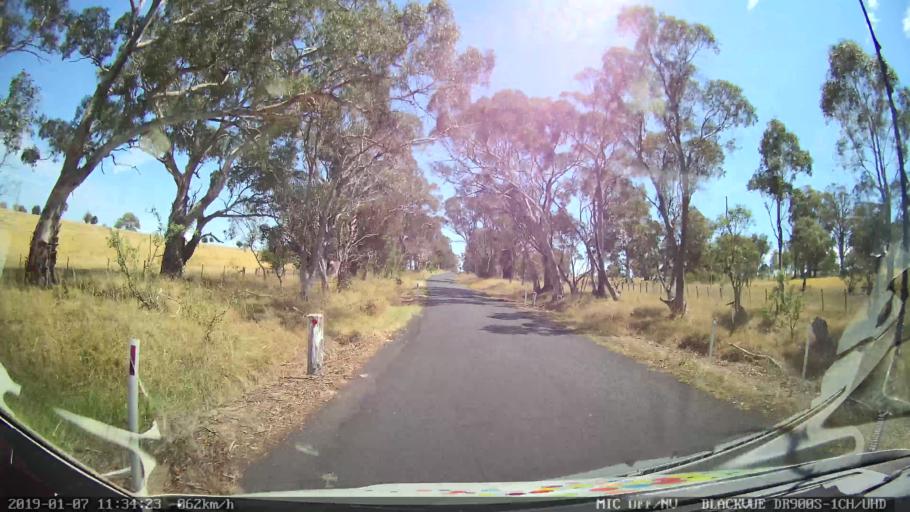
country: AU
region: New South Wales
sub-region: Armidale Dumaresq
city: Armidale
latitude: -30.3904
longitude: 151.5590
